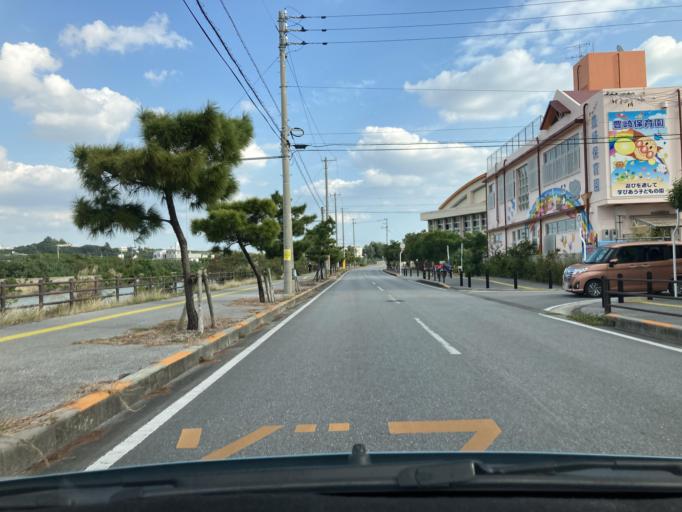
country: JP
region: Okinawa
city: Tomigusuku
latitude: 26.1591
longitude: 127.6629
